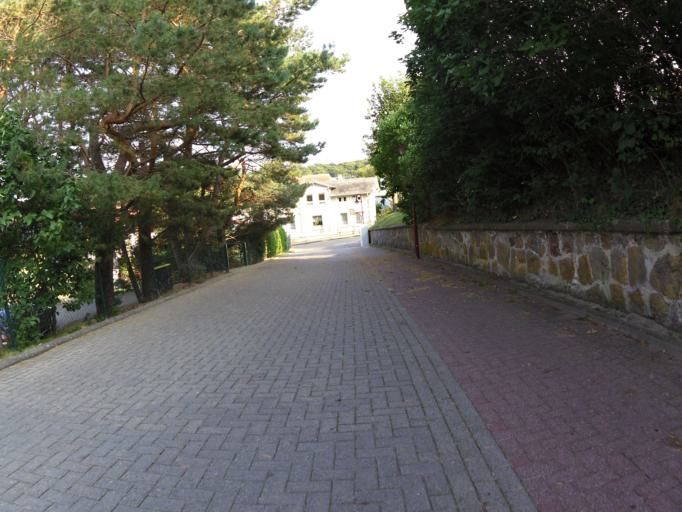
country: DE
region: Mecklenburg-Vorpommern
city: Seebad Heringsdorf
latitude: 53.9559
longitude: 14.1515
